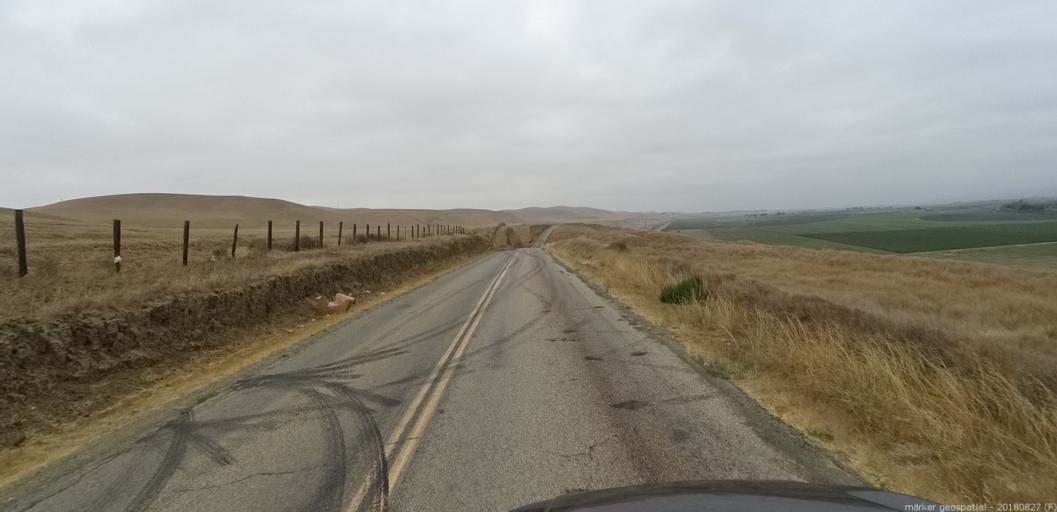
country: US
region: California
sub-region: Monterey County
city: Greenfield
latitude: 36.3169
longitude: -121.1744
